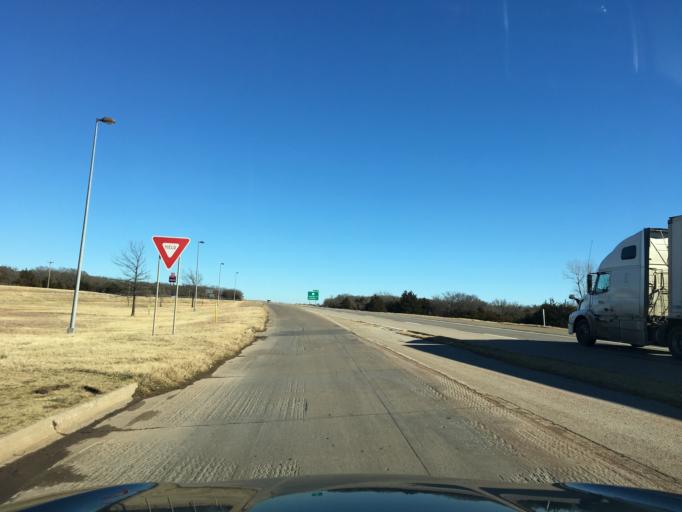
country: US
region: Oklahoma
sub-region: Pawnee County
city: Pawnee
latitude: 36.2244
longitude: -96.7952
